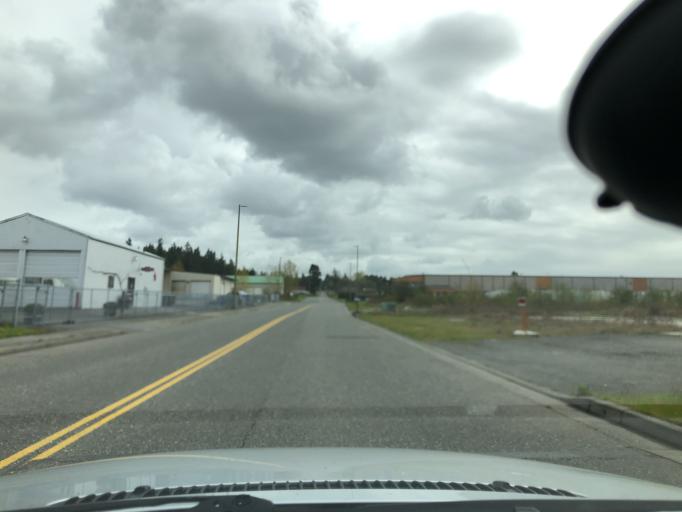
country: US
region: Washington
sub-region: Whatcom County
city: Blaine
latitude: 48.9905
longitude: -122.7310
